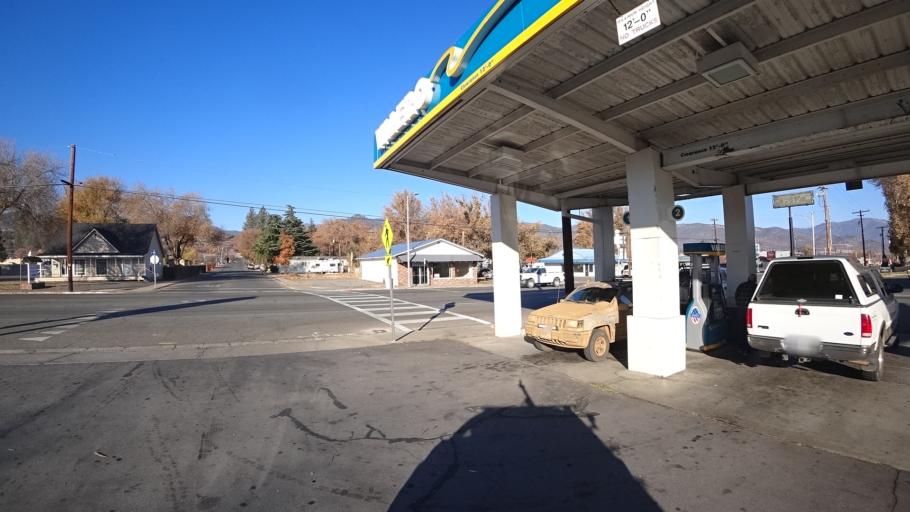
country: US
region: California
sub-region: Siskiyou County
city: Yreka
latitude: 41.7185
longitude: -122.6394
